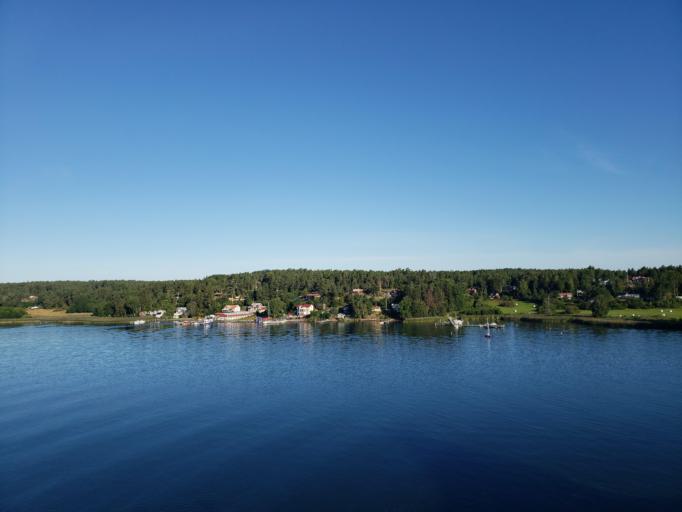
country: SE
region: Stockholm
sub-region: Vaxholms Kommun
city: Vaxholm
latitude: 59.5011
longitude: 18.4703
